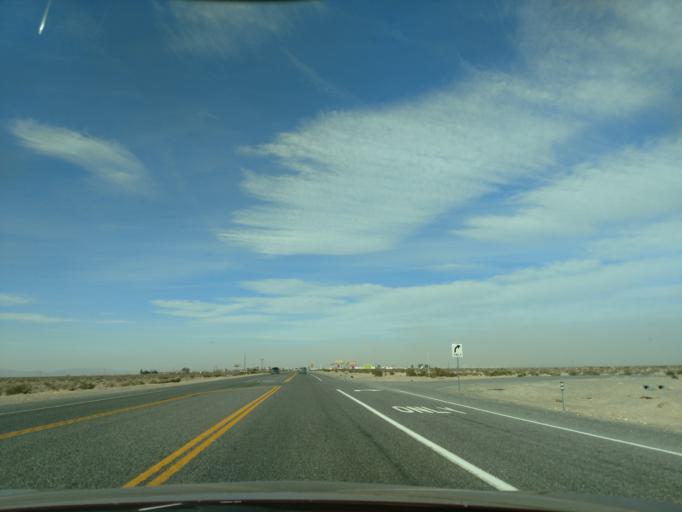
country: US
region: Nevada
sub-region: Nye County
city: Beatty
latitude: 36.6403
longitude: -116.3859
